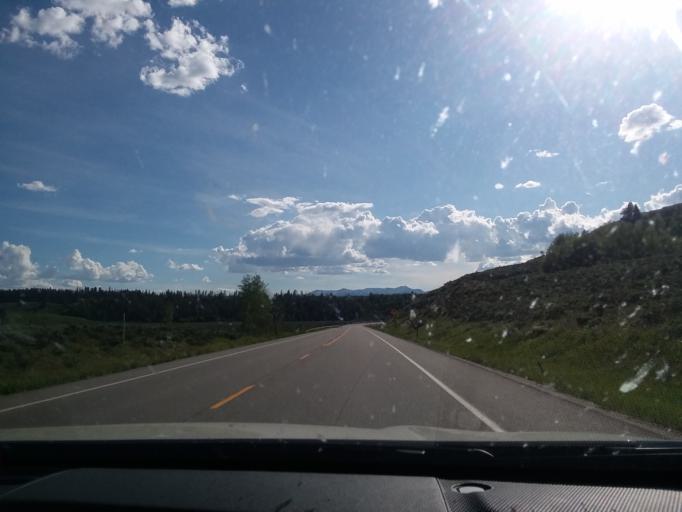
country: US
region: Wyoming
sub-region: Sublette County
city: Pinedale
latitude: 43.1497
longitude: -110.2614
